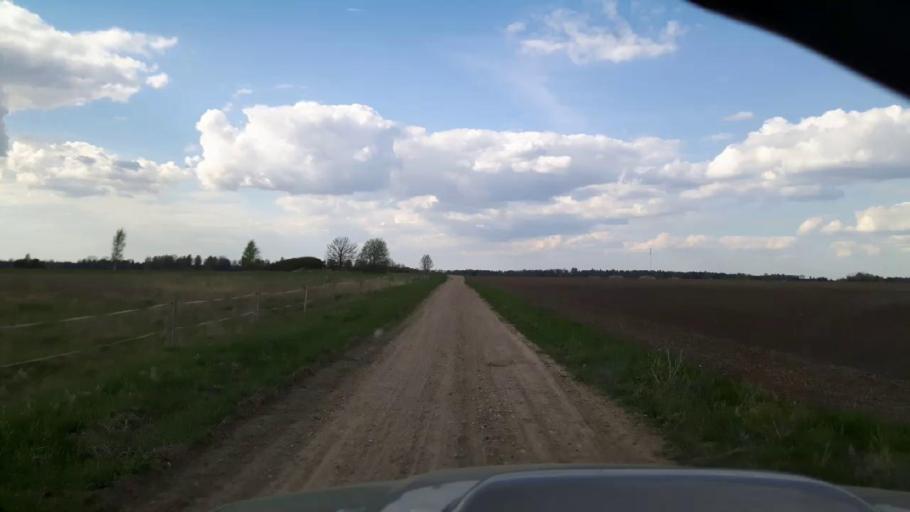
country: EE
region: Paernumaa
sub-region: Sindi linn
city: Sindi
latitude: 58.4335
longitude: 24.7700
